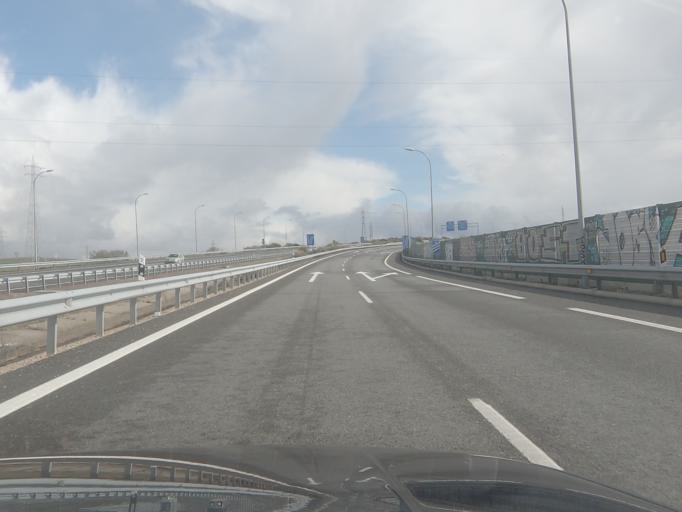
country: ES
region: Castille and Leon
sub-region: Provincia de Salamanca
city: Villamayor
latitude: 41.0012
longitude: -5.6768
